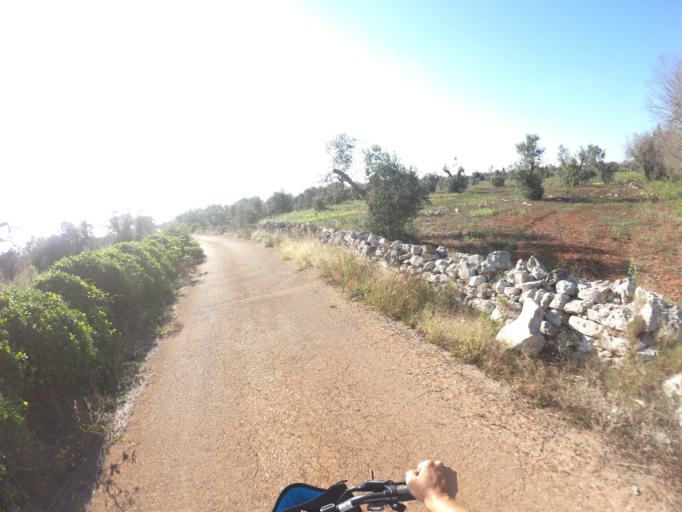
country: IT
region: Apulia
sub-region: Provincia di Lecce
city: Casarano
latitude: 40.0423
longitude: 18.1963
